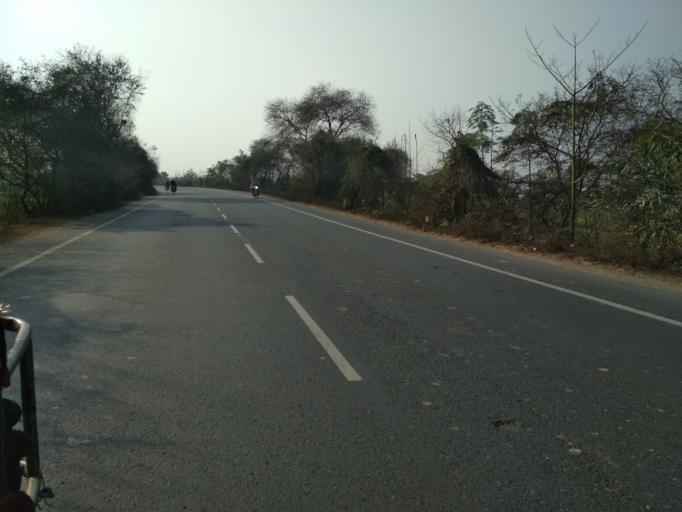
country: IN
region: Bihar
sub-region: Khagaria
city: Khagaria
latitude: 25.5080
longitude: 86.5461
